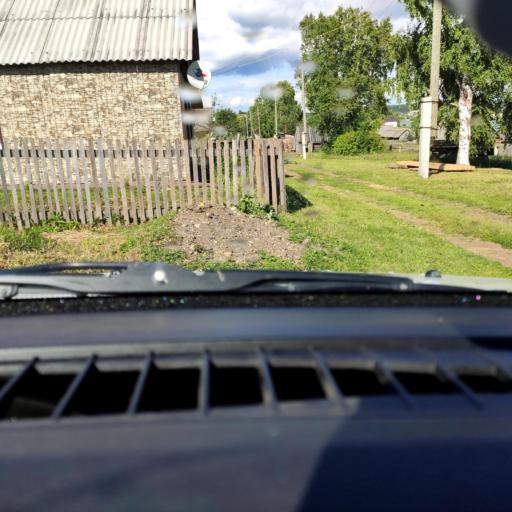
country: RU
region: Perm
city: Uinskoye
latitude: 57.1142
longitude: 56.5044
